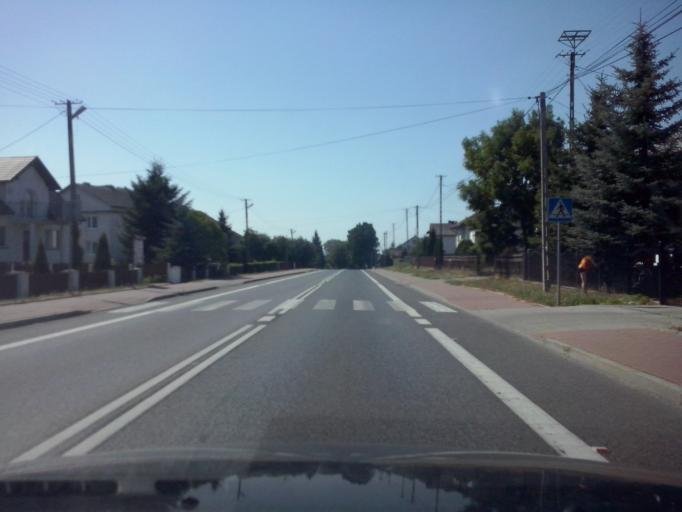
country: PL
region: Swietokrzyskie
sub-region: Powiat kielecki
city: Bieliny
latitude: 50.8491
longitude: 20.9074
